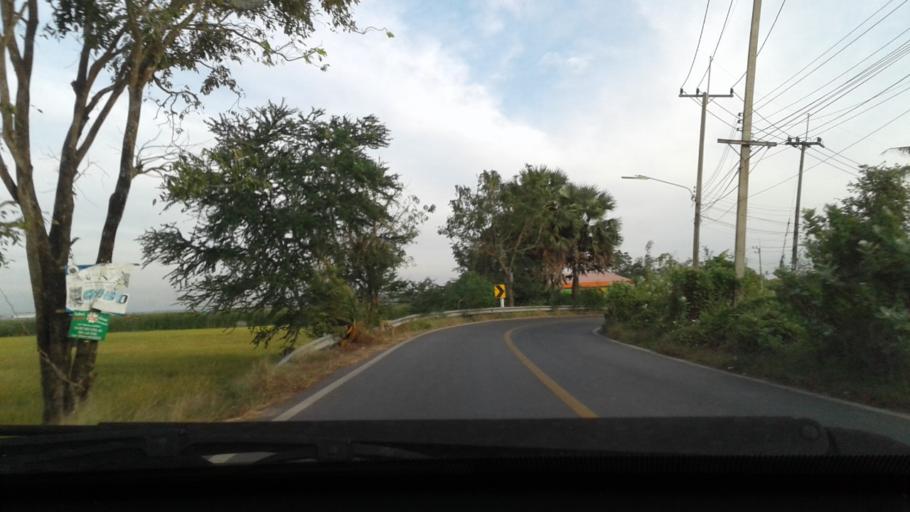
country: TH
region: Nonthaburi
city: Sai Noi
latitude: 13.9182
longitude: 100.2548
